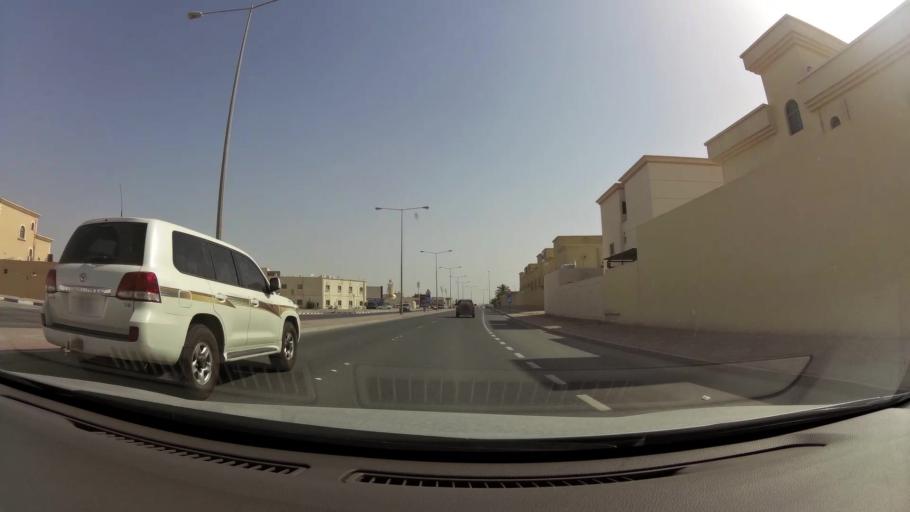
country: QA
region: Baladiyat ar Rayyan
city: Ar Rayyan
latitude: 25.3574
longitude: 51.4386
